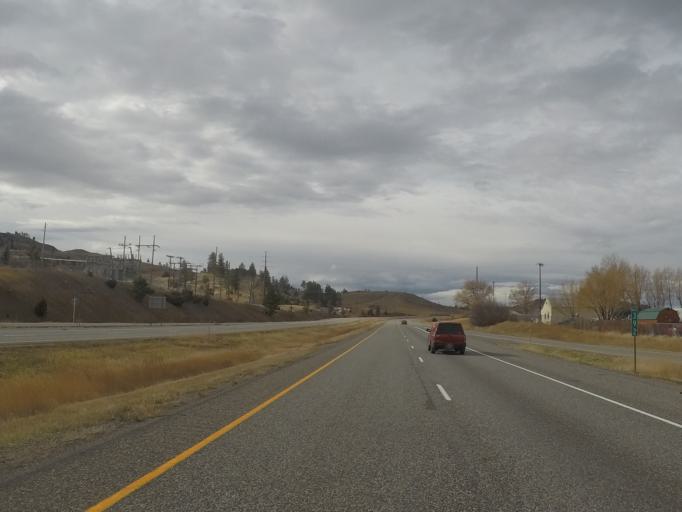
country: US
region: Montana
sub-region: Stillwater County
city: Absarokee
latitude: 45.7048
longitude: -109.5439
